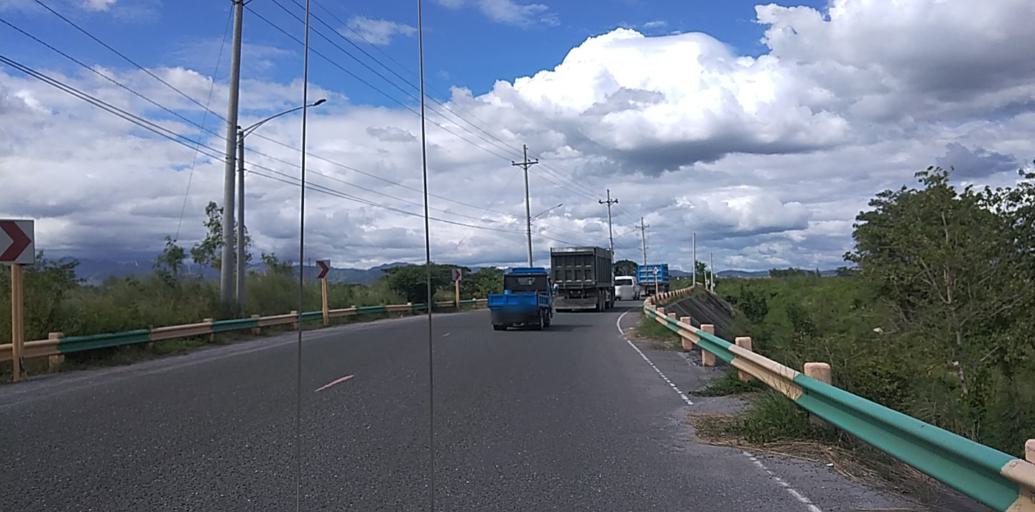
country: PH
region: Central Luzon
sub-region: Province of Pampanga
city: Dolores
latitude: 15.0870
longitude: 120.5398
